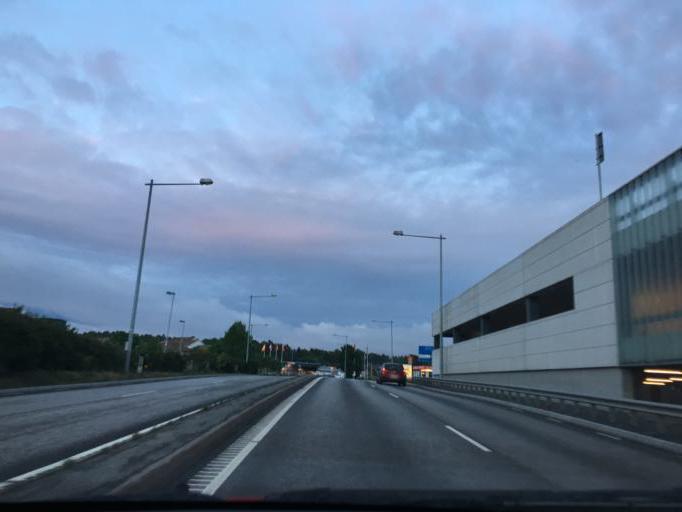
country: SE
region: Stockholm
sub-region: Osterakers Kommun
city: Akersberga
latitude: 59.4794
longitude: 18.3024
